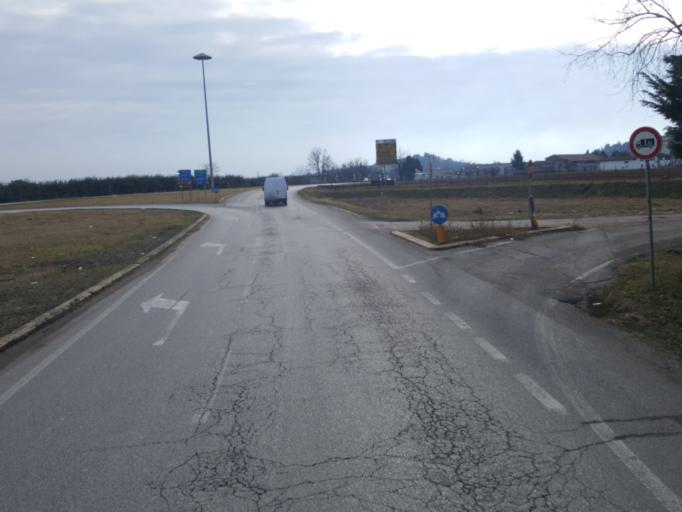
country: IT
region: Veneto
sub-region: Provincia di Verona
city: Sona
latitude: 45.4391
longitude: 10.8506
